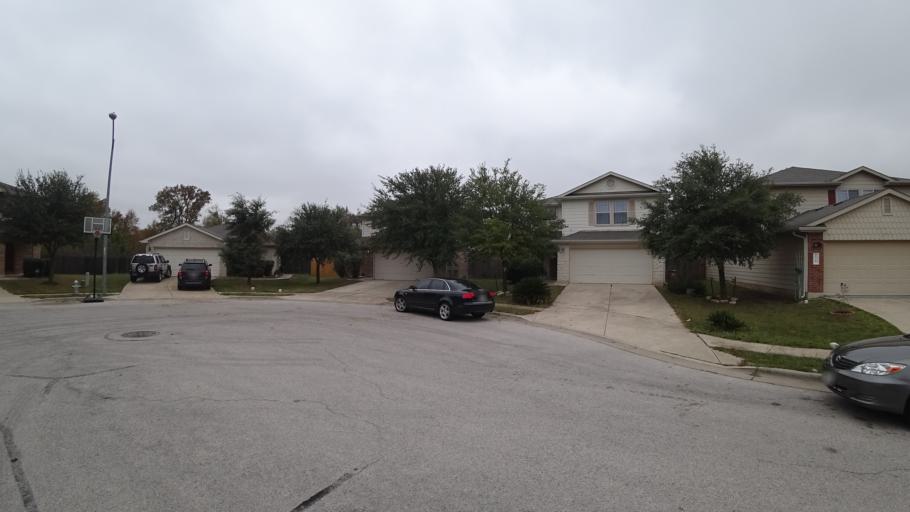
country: US
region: Texas
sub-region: Travis County
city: Pflugerville
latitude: 30.3740
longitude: -97.6147
